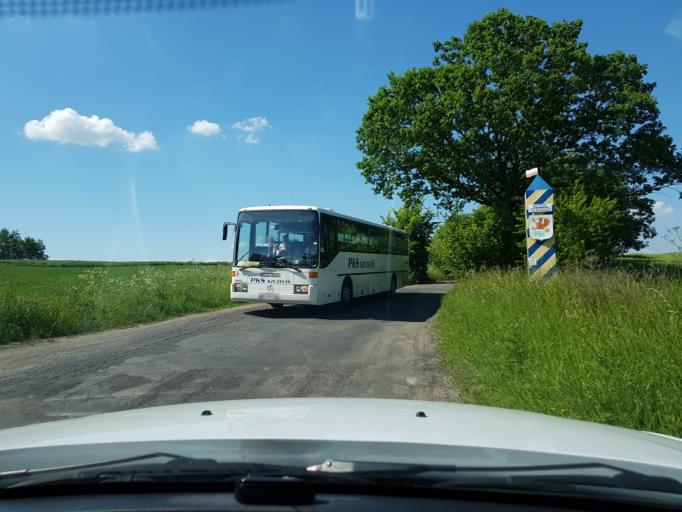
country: PL
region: West Pomeranian Voivodeship
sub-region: Powiat gryfinski
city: Gryfino
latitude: 53.1425
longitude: 14.5400
